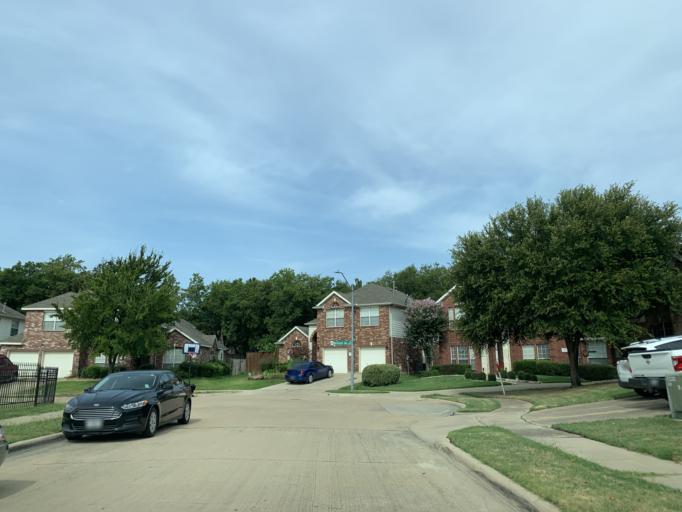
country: US
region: Texas
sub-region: Dallas County
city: Grand Prairie
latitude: 32.6634
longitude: -97.0061
